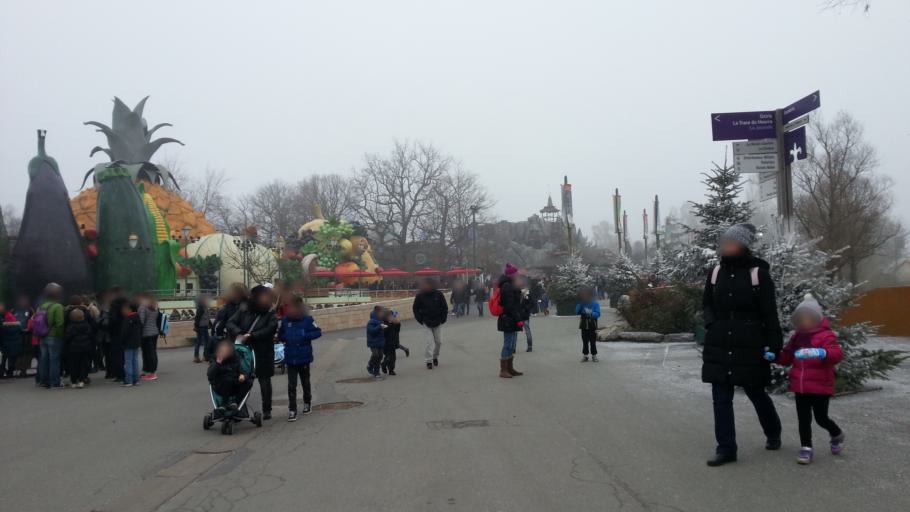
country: FR
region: Picardie
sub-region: Departement de l'Oise
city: Thiers-sur-Theve
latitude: 49.1327
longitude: 2.5709
